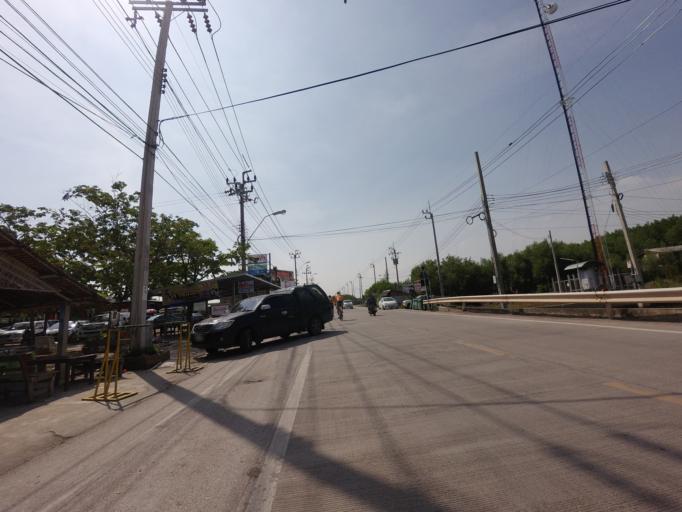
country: TH
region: Bangkok
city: Thung Khru
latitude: 13.5264
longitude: 100.4194
